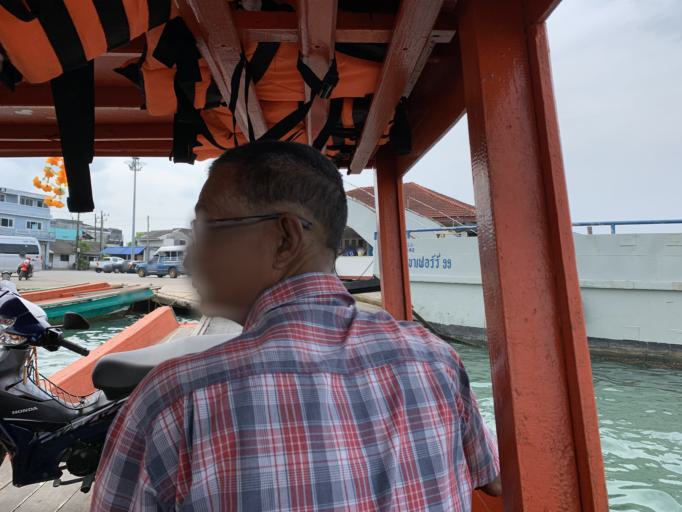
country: TH
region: Phangnga
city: Takua Pa
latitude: 8.8658
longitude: 98.2738
